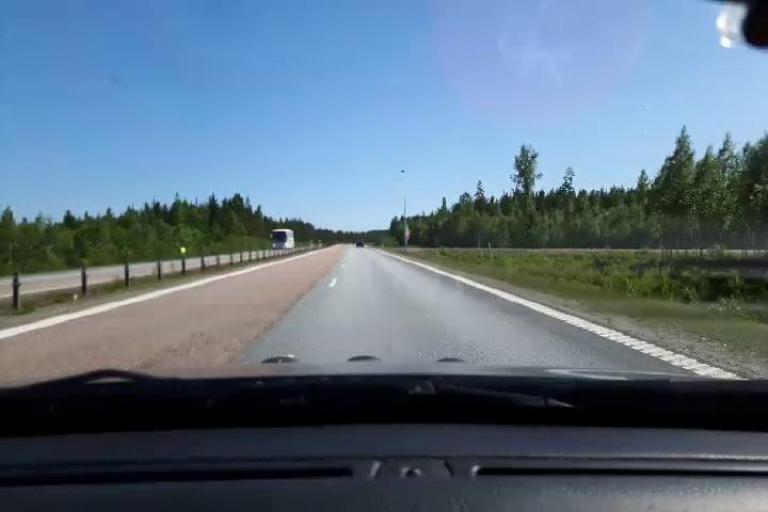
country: SE
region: Gaevleborg
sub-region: Soderhamns Kommun
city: Soderhamn
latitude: 61.4142
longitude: 16.9897
